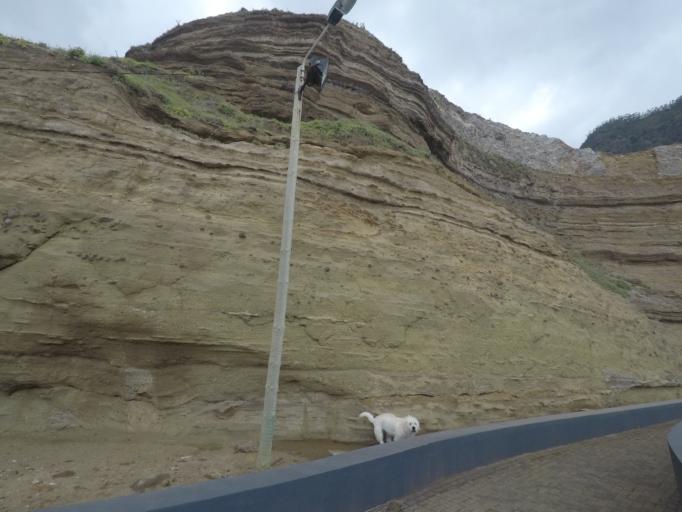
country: PT
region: Madeira
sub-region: Santana
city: Santana
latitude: 32.7748
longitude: -16.8266
